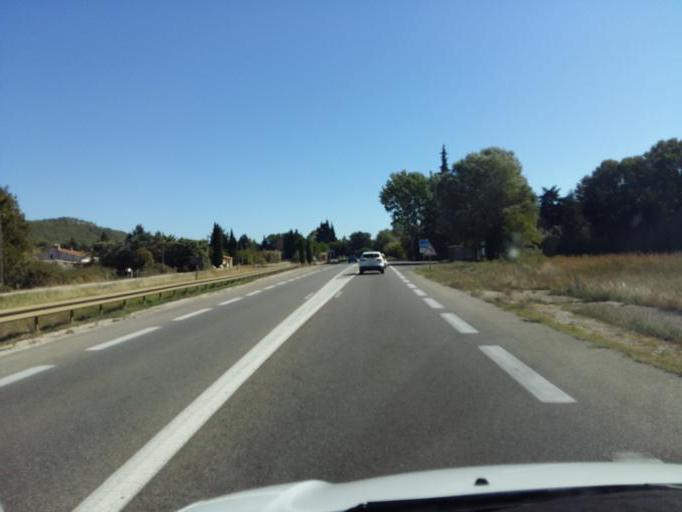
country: FR
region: Provence-Alpes-Cote d'Azur
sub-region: Departement des Bouches-du-Rhone
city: Mallemort
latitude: 43.7566
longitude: 5.1487
